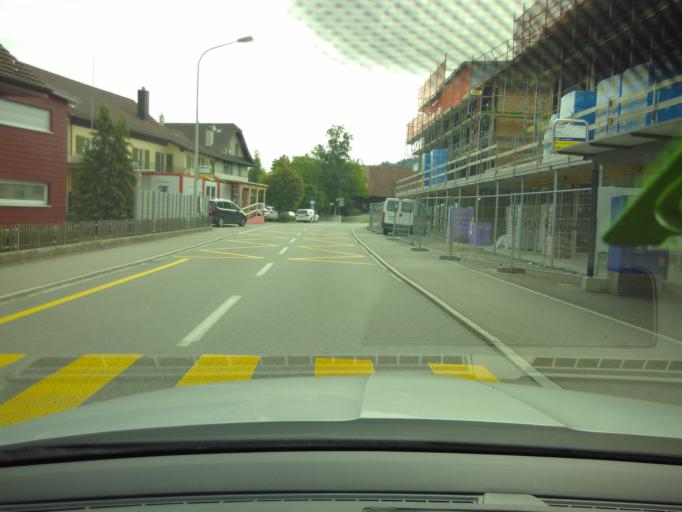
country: CH
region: Lucerne
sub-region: Sursee District
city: Gunzwil
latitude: 47.2199
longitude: 8.1535
